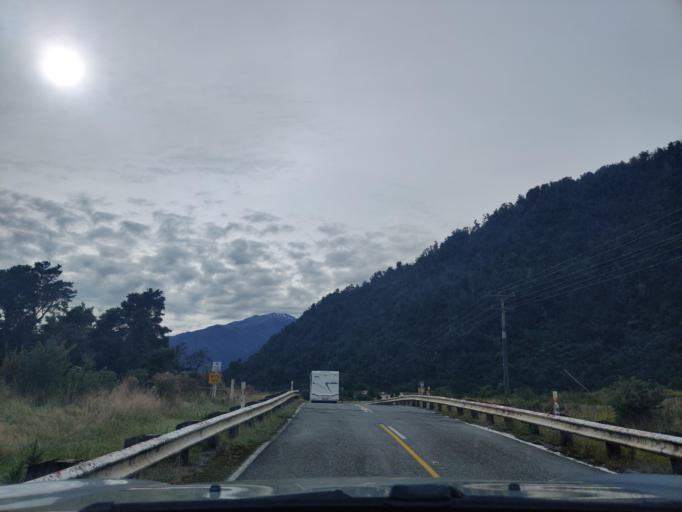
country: NZ
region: West Coast
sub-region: Westland District
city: Hokitika
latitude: -43.2800
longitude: 170.3385
